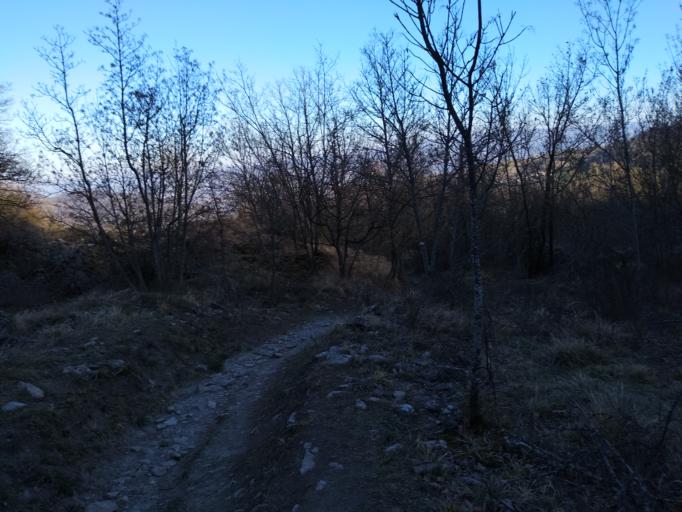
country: IT
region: Emilia-Romagna
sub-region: Provincia di Reggio Emilia
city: Castelnovo ne'Monti
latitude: 44.4240
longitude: 10.4201
